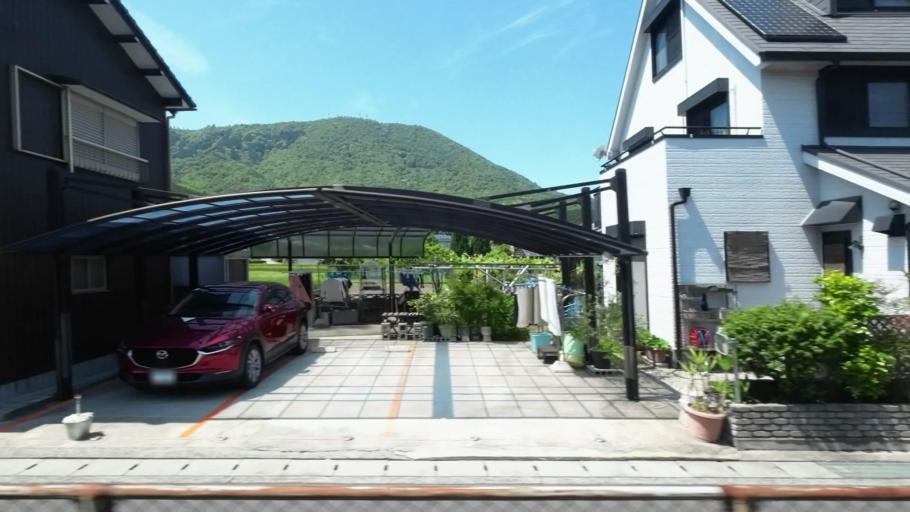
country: JP
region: Kagawa
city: Marugame
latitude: 34.2110
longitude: 133.8030
